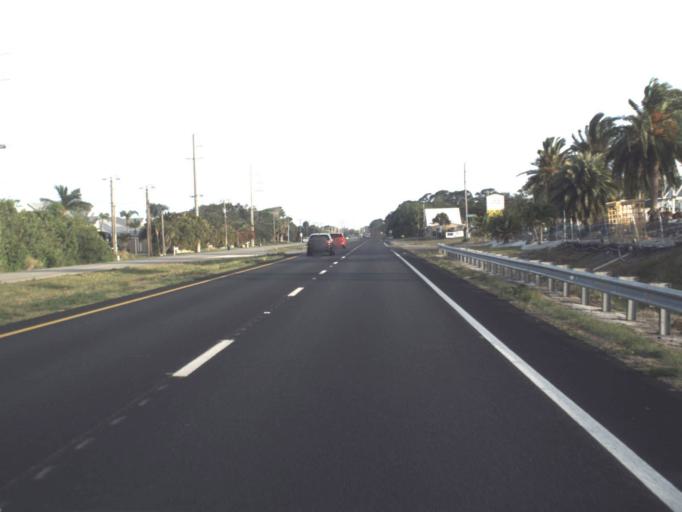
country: US
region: Florida
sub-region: Brevard County
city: South Patrick Shores
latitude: 28.2362
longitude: -80.6760
